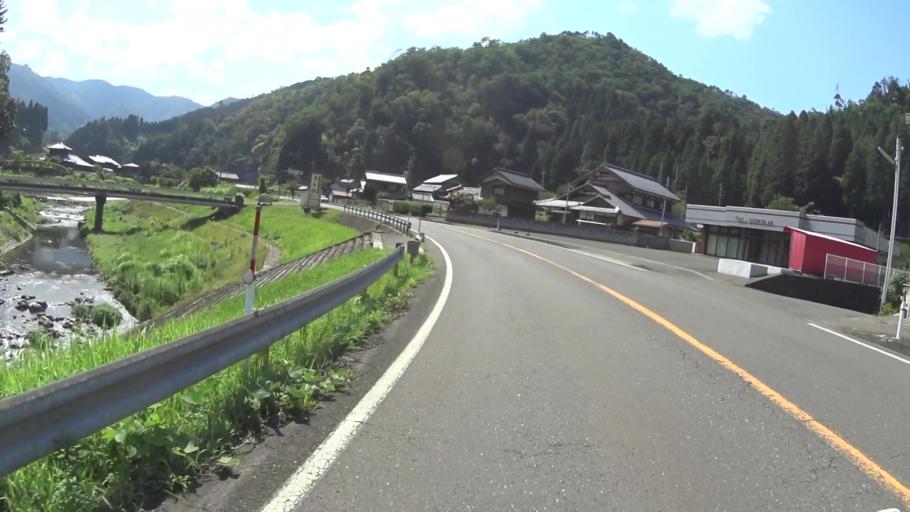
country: JP
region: Fukui
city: Obama
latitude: 35.3956
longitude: 135.5874
